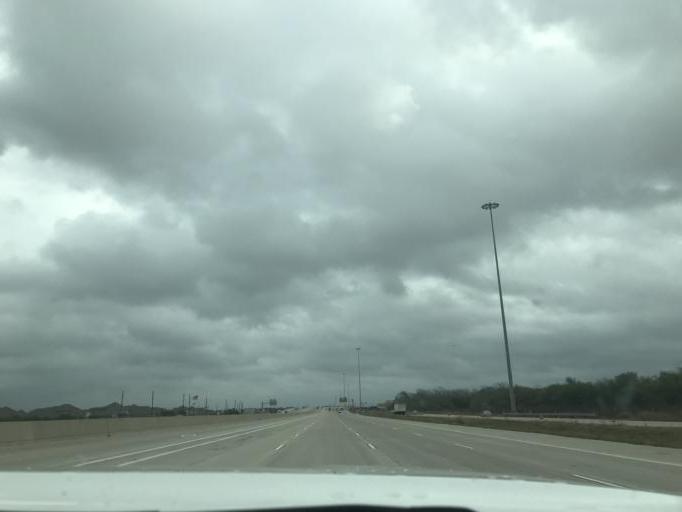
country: US
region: Texas
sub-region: Fort Bend County
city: Richmond
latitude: 29.5539
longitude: -95.7254
